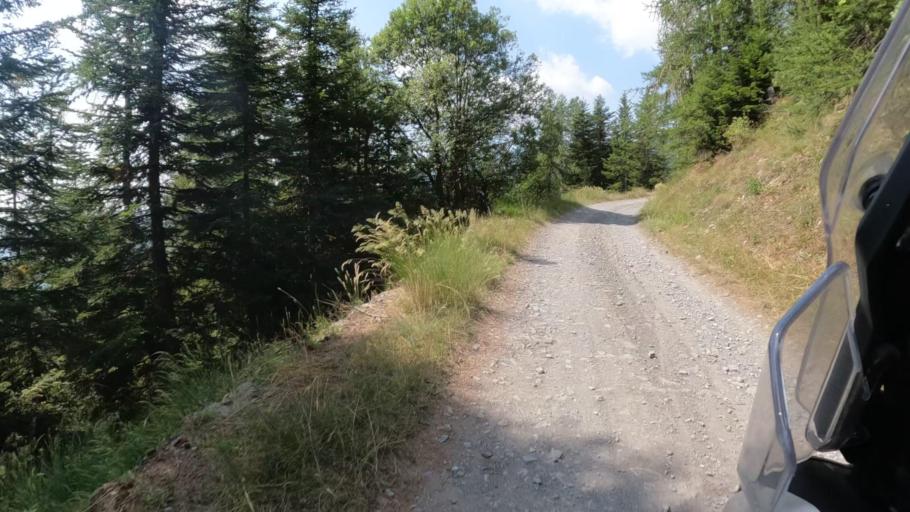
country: IT
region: Piedmont
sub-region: Provincia di Cuneo
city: Briga Alta
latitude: 44.0359
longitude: 7.6827
